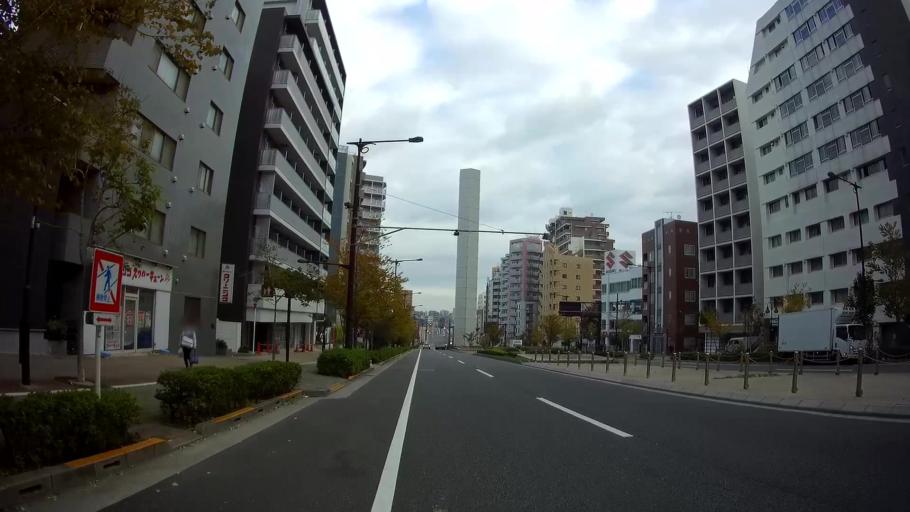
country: JP
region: Tokyo
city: Tokyo
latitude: 35.7112
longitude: 139.6853
